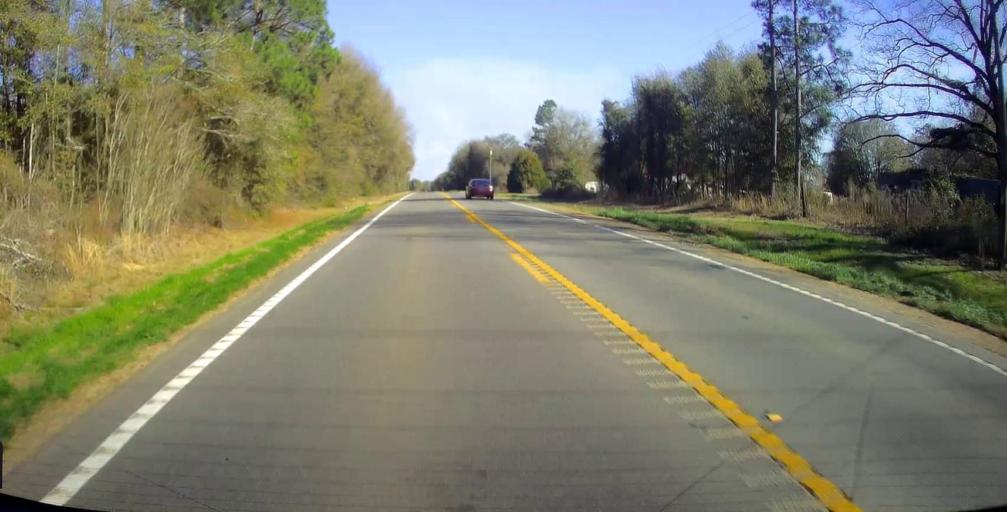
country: US
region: Georgia
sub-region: Macon County
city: Oglethorpe
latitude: 32.3325
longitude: -84.1042
